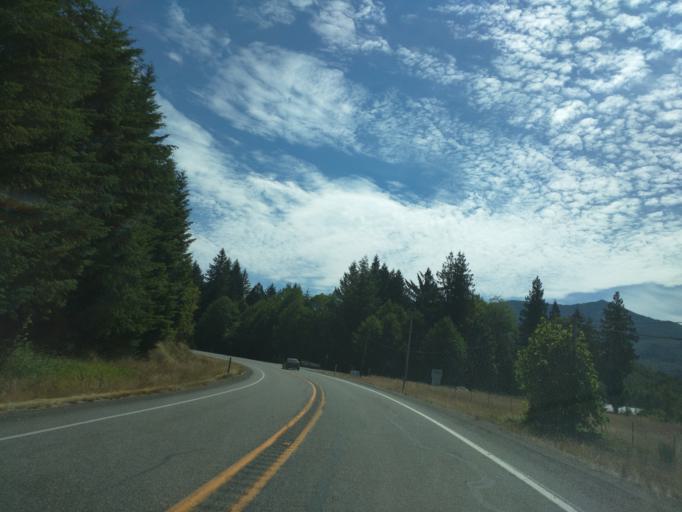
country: US
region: Washington
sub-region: Whatcom County
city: Peaceful Valley
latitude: 48.9159
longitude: -122.1209
